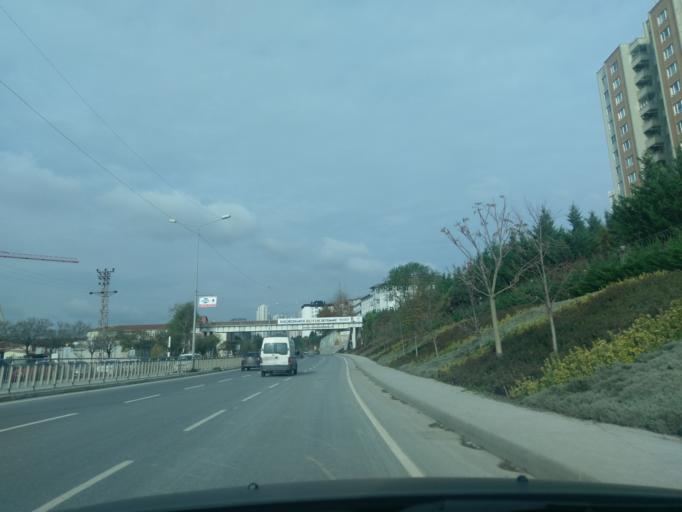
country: TR
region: Istanbul
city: Basaksehir
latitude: 41.0519
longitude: 28.7746
